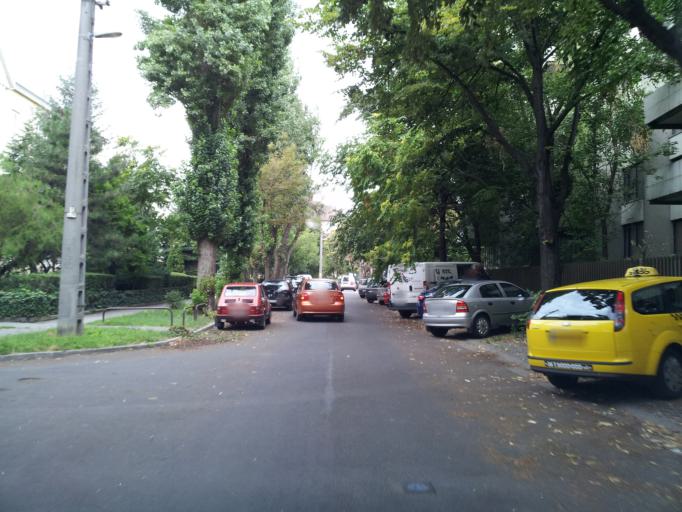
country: HU
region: Budapest
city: Budapest XIV. keruelet
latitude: 47.5041
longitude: 19.1053
